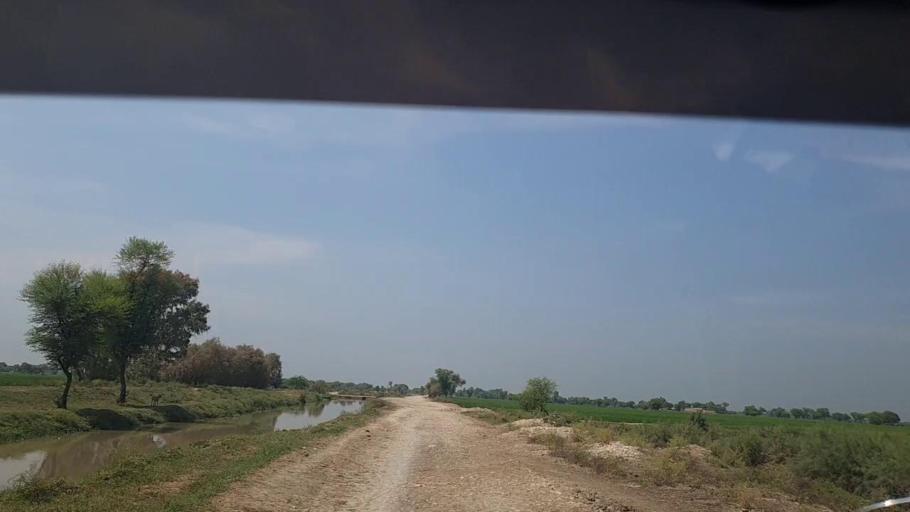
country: PK
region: Sindh
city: Thul
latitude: 28.1944
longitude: 68.7085
